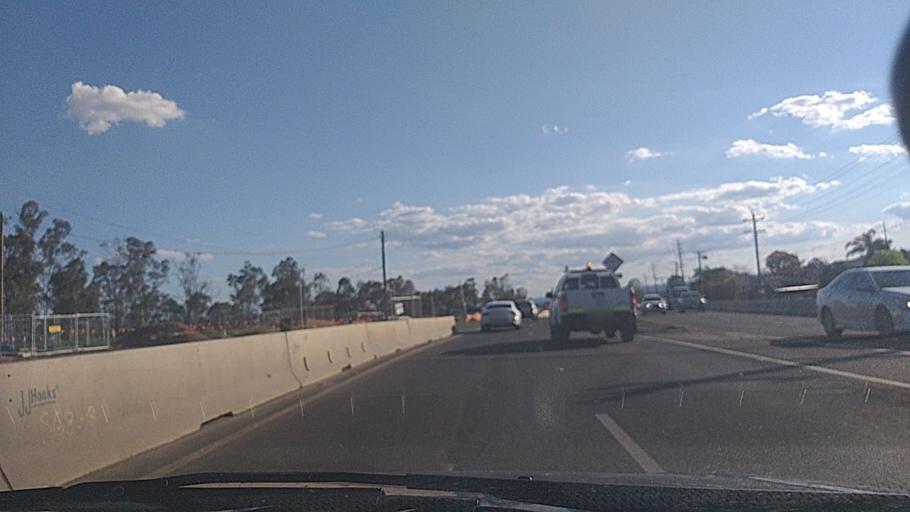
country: AU
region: New South Wales
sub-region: Penrith Municipality
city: Kingswood Park
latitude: -33.7807
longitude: 150.7102
